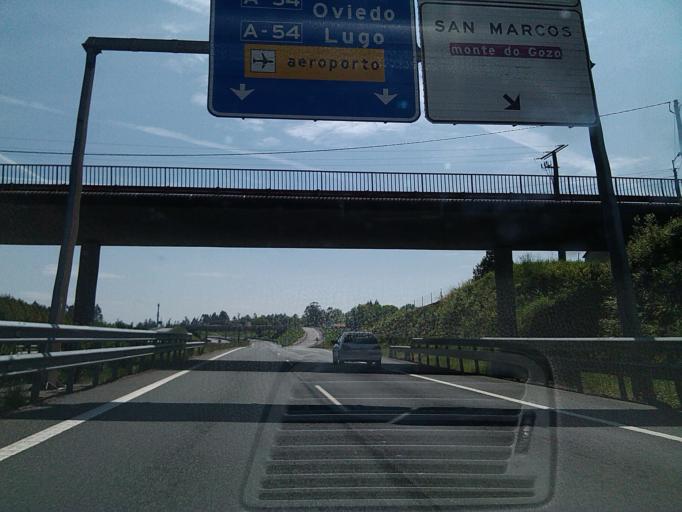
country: ES
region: Galicia
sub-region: Provincia da Coruna
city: Santiago de Compostela
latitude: 42.8988
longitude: -8.4879
